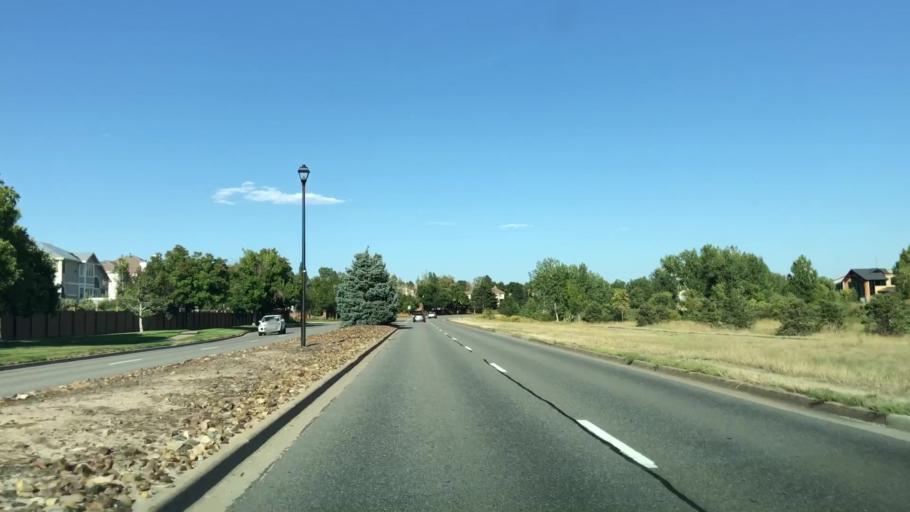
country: US
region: Colorado
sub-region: Arapahoe County
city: Dove Valley
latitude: 39.6109
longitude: -104.7995
